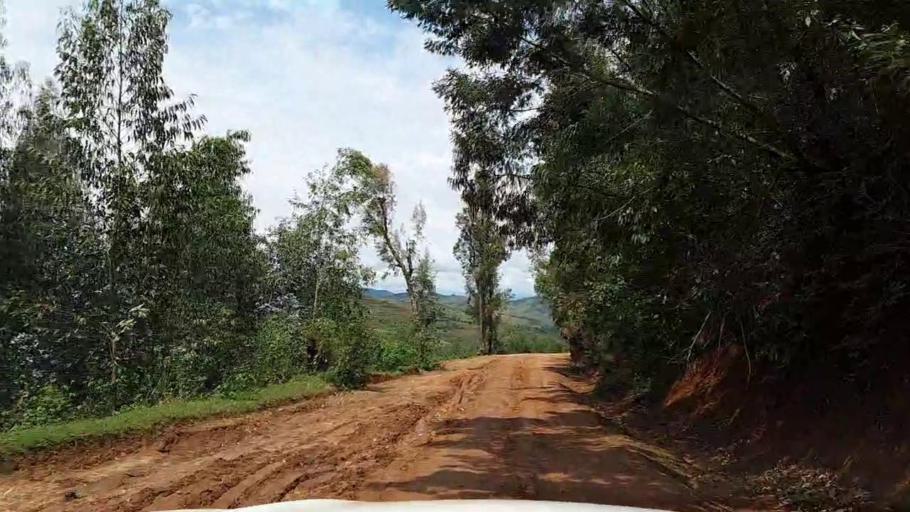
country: RW
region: Southern Province
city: Gikongoro
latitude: -2.3391
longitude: 29.5168
